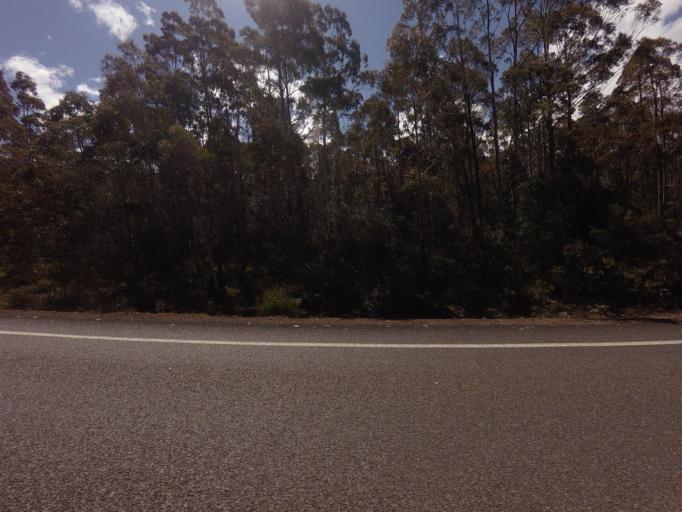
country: AU
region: Tasmania
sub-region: Northern Midlands
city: Evandale
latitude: -42.0165
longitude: 147.8574
